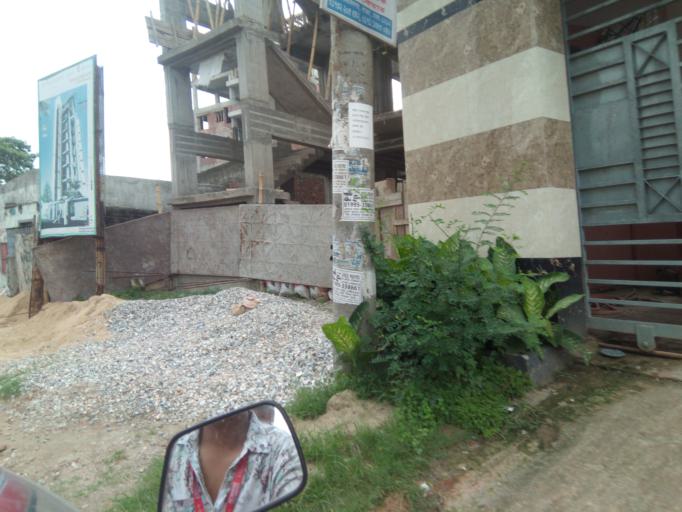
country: BD
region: Dhaka
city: Paltan
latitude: 23.7649
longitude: 90.4342
